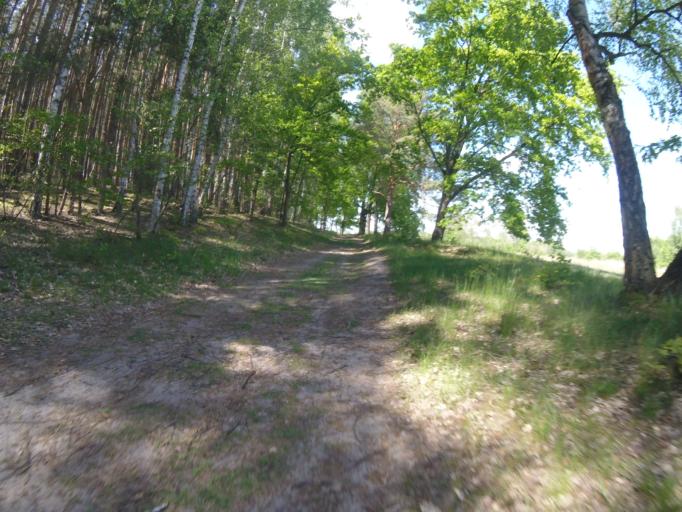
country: DE
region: Brandenburg
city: Teupitz
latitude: 52.1180
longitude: 13.6036
